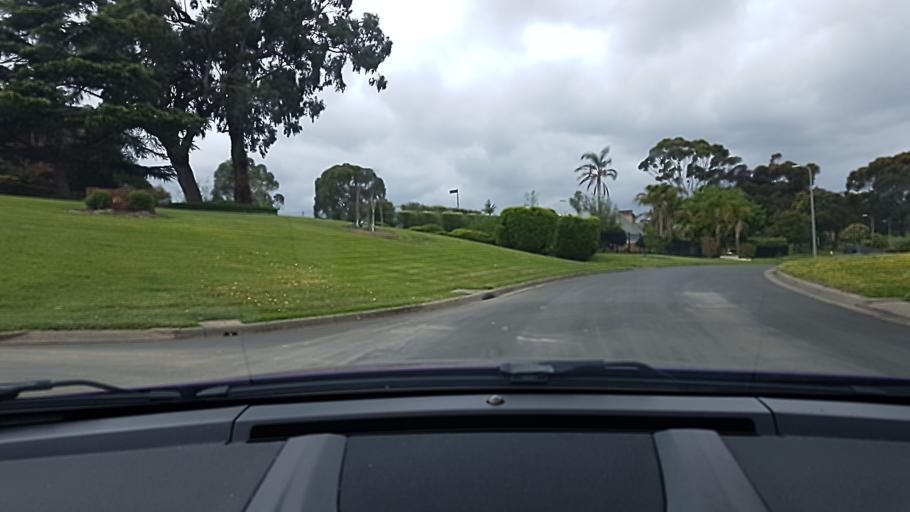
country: AU
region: Victoria
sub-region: Nillumbik
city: Eltham
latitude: -37.7490
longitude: 145.1402
